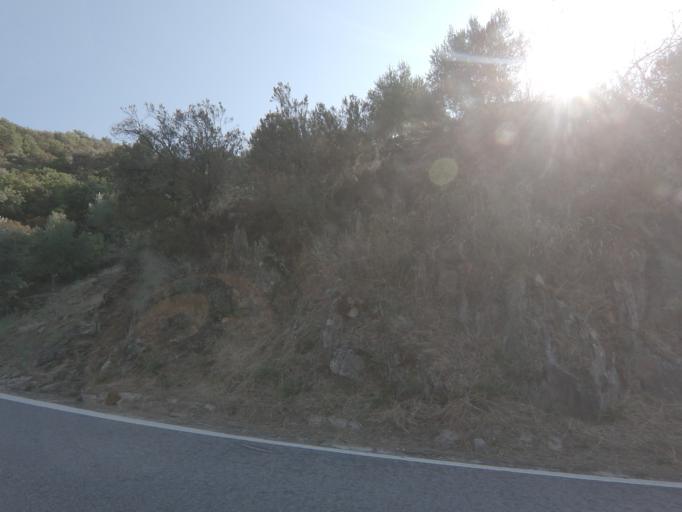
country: PT
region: Viseu
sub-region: Tabuaco
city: Tabuaco
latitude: 41.1444
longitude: -7.5757
